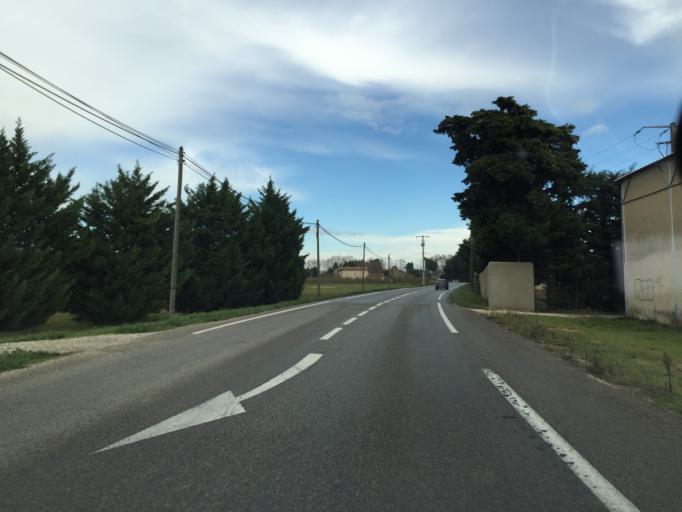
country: FR
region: Provence-Alpes-Cote d'Azur
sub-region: Departement du Vaucluse
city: L'Isle-sur-la-Sorgue
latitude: 43.8758
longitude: 5.0431
